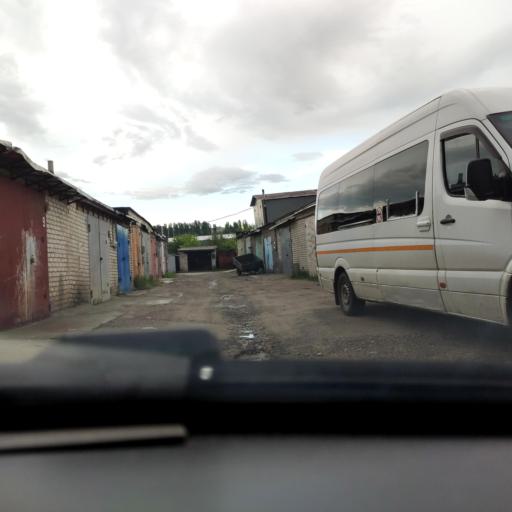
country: RU
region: Voronezj
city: Podgornoye
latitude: 51.7013
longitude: 39.1278
